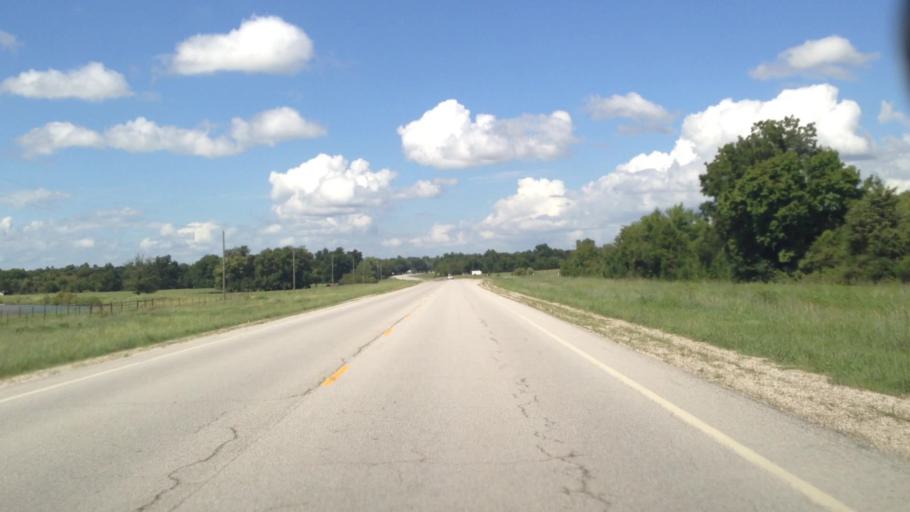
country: US
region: Kansas
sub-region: Labette County
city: Chetopa
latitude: 37.0193
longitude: -95.0868
